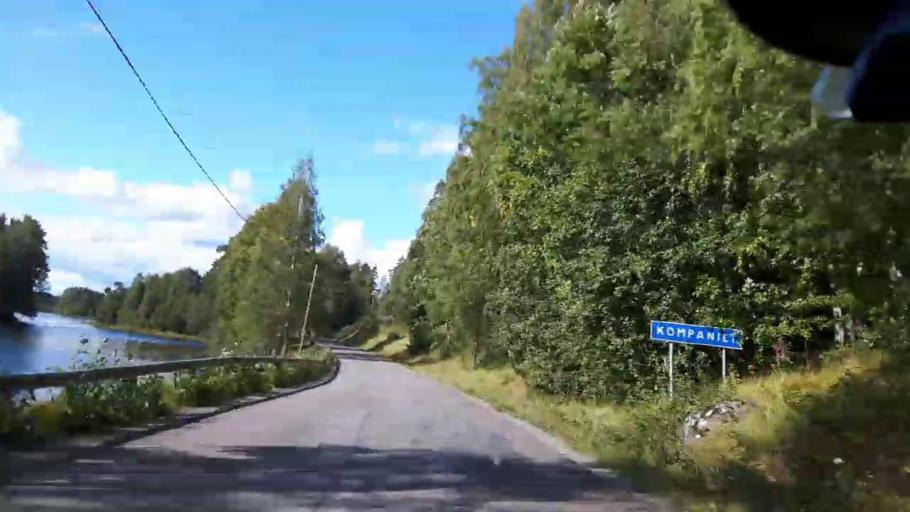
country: SE
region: Jaemtland
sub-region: Braecke Kommun
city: Braecke
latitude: 63.1773
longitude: 15.5598
